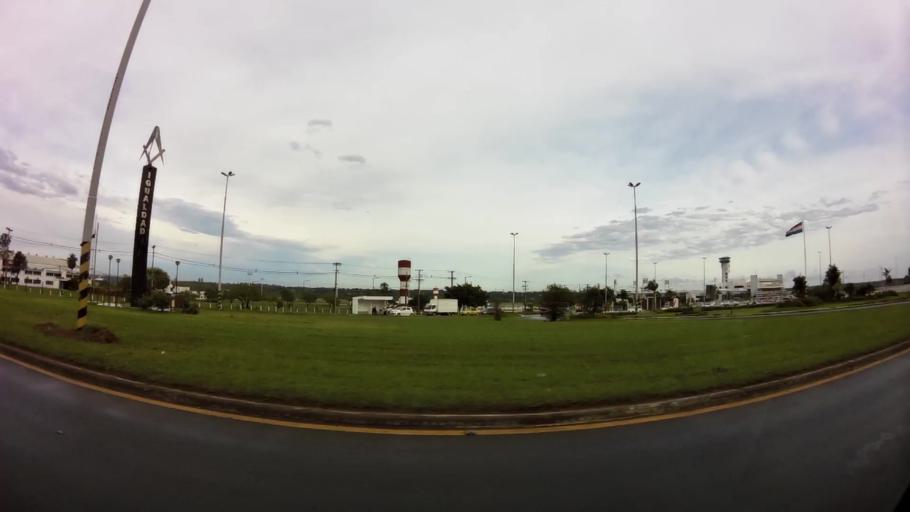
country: PY
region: Central
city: Limpio
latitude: -25.2447
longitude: -57.5113
